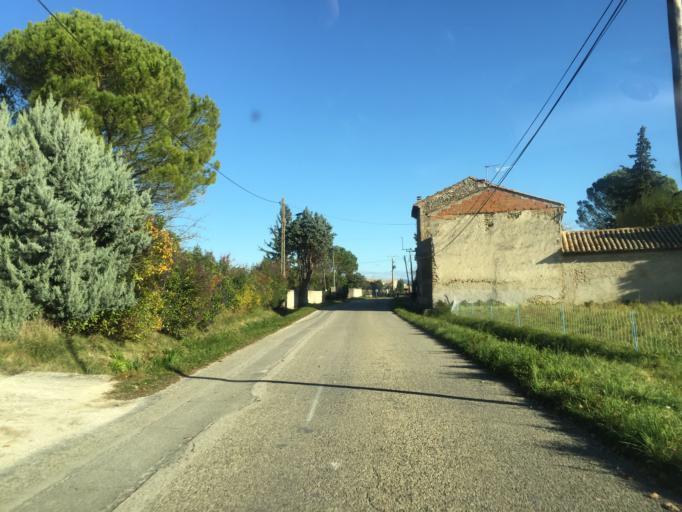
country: FR
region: Provence-Alpes-Cote d'Azur
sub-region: Departement du Vaucluse
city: Courthezon
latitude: 44.0939
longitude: 4.8961
